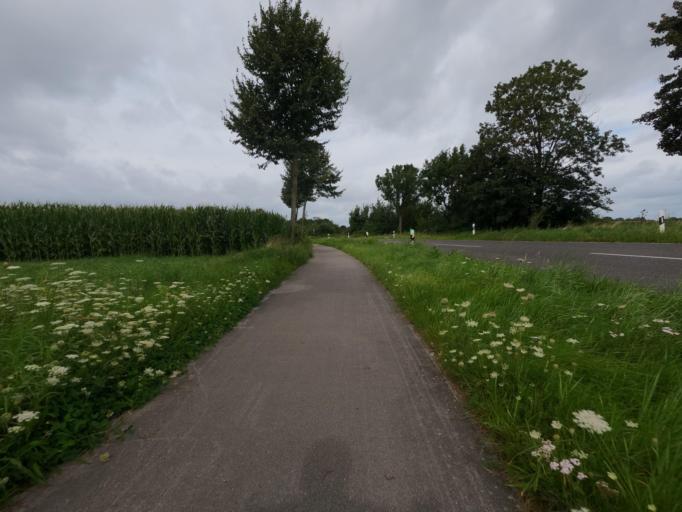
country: DE
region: North Rhine-Westphalia
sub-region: Regierungsbezirk Koln
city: Heinsberg
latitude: 51.0326
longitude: 6.1539
